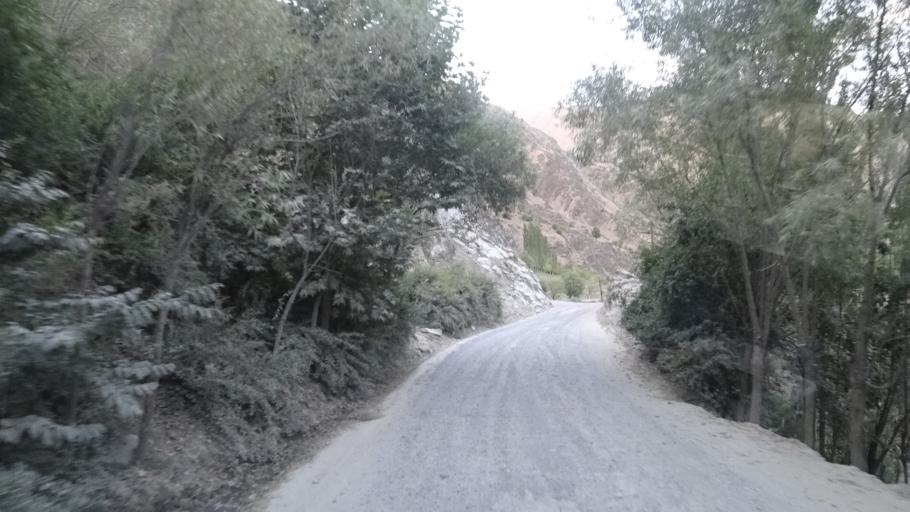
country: AF
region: Badakhshan
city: Nusay
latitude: 38.4537
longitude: 70.8228
